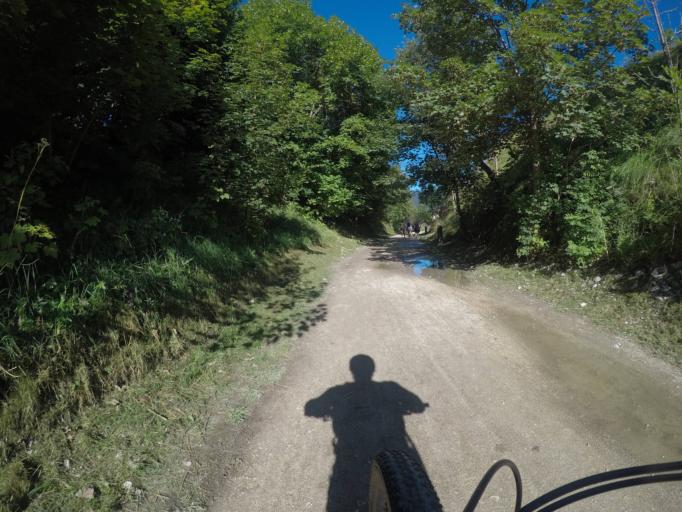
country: IT
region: Veneto
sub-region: Provincia di Vicenza
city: Canove di Roana
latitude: 45.8673
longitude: 11.4860
